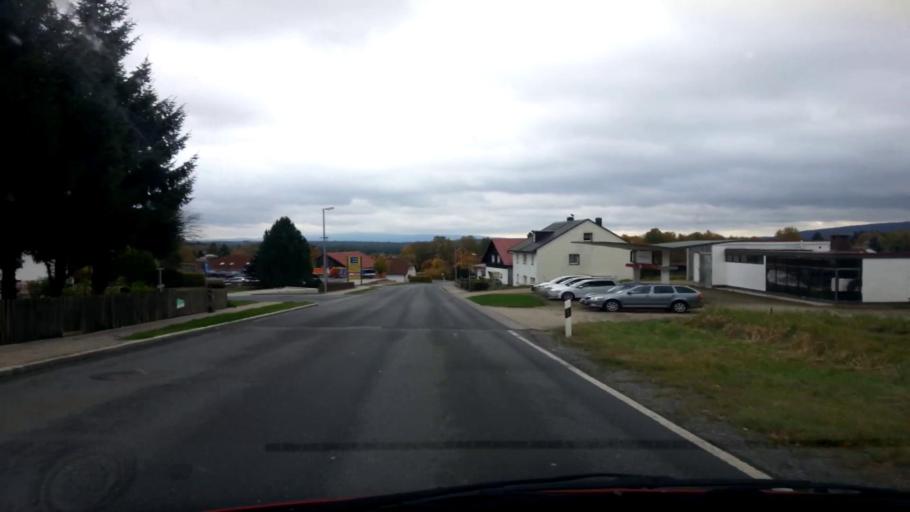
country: DE
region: Bavaria
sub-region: Upper Franconia
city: Fichtelberg
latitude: 50.0004
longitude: 11.8450
